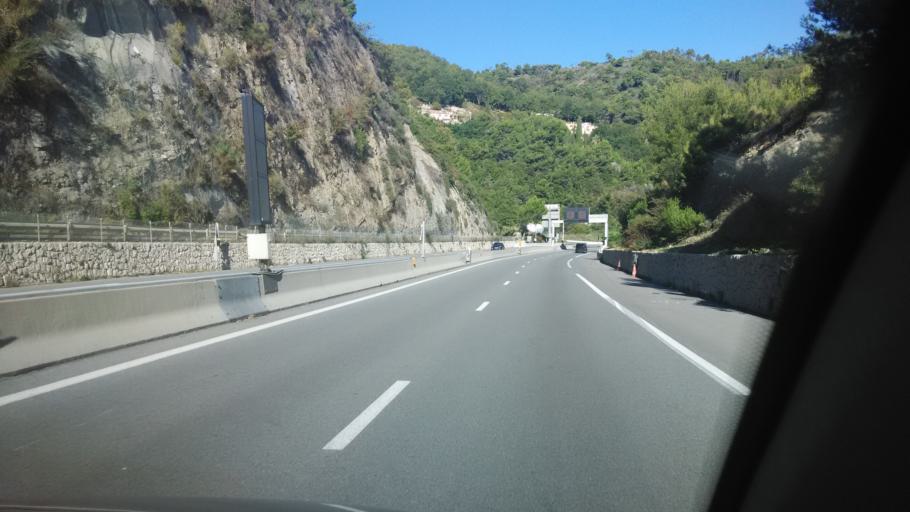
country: FR
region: Provence-Alpes-Cote d'Azur
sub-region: Departement des Alpes-Maritimes
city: Gorbio
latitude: 43.7677
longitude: 7.4497
